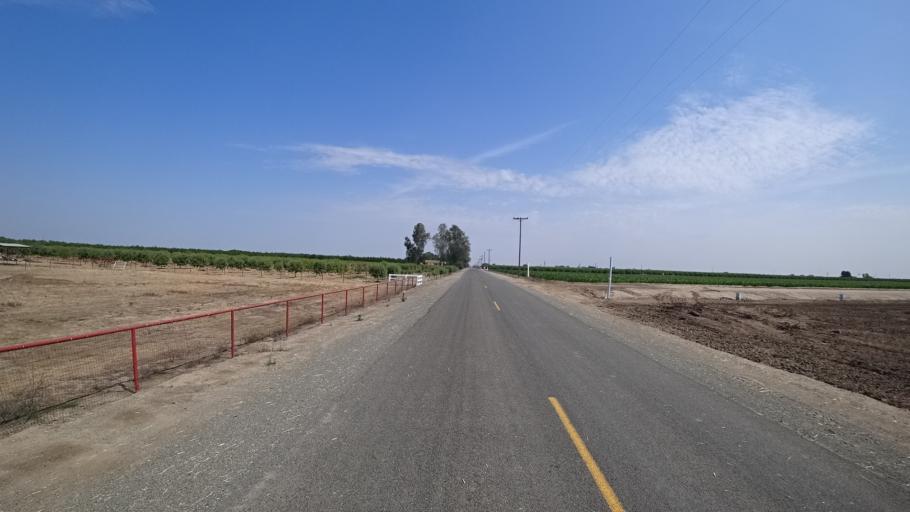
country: US
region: California
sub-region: Fresno County
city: Riverdale
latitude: 36.3979
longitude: -119.7983
